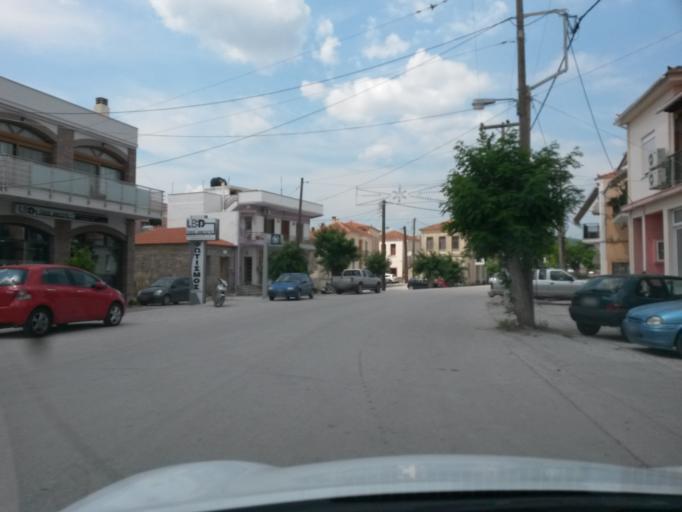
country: GR
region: North Aegean
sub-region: Nomos Lesvou
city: Kalloni
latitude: 39.2306
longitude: 26.2062
